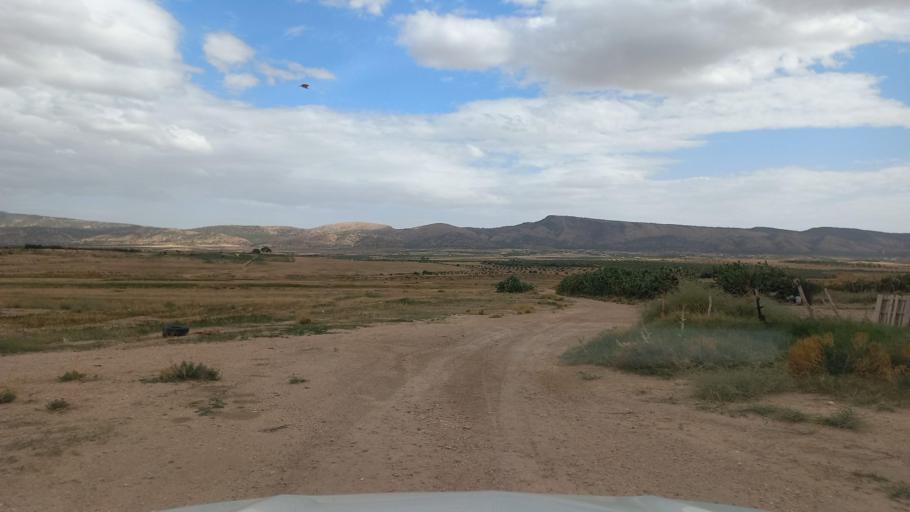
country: TN
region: Al Qasrayn
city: Sbiba
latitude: 35.3791
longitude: 9.1187
